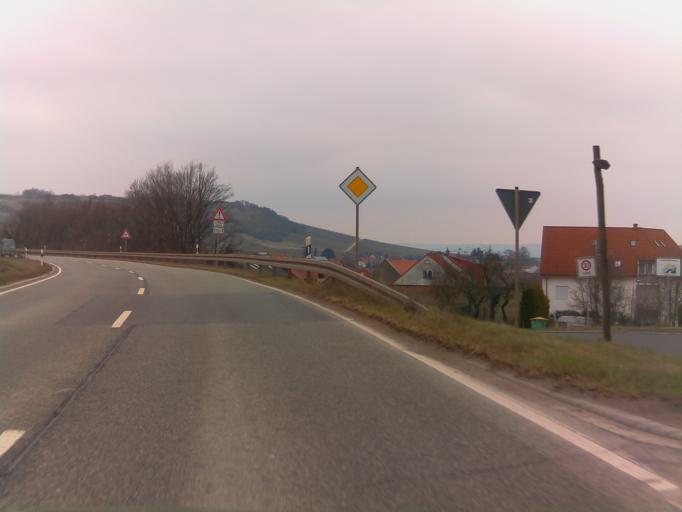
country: DE
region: Rheinland-Pfalz
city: Frei-Laubersheim
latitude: 49.7978
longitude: 7.8956
